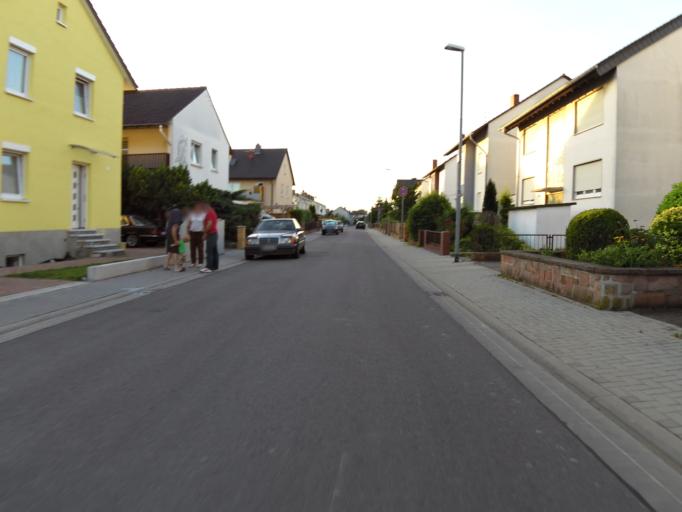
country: DE
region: Rheinland-Pfalz
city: Beindersheim
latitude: 49.5601
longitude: 8.3271
